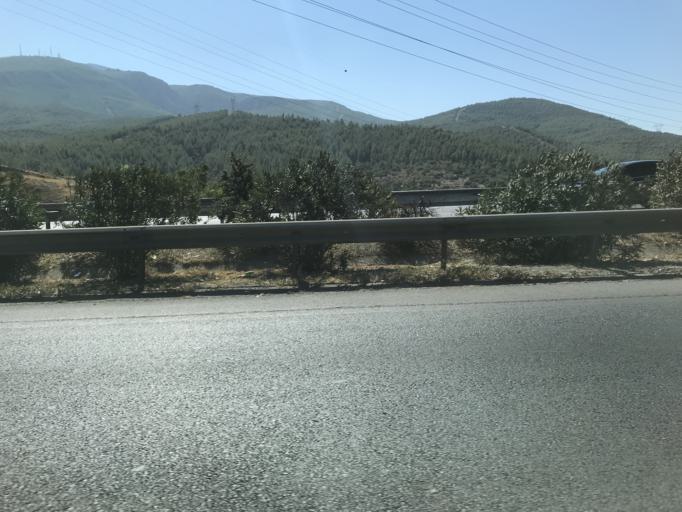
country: TR
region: Izmir
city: Buca
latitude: 38.4062
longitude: 27.2332
